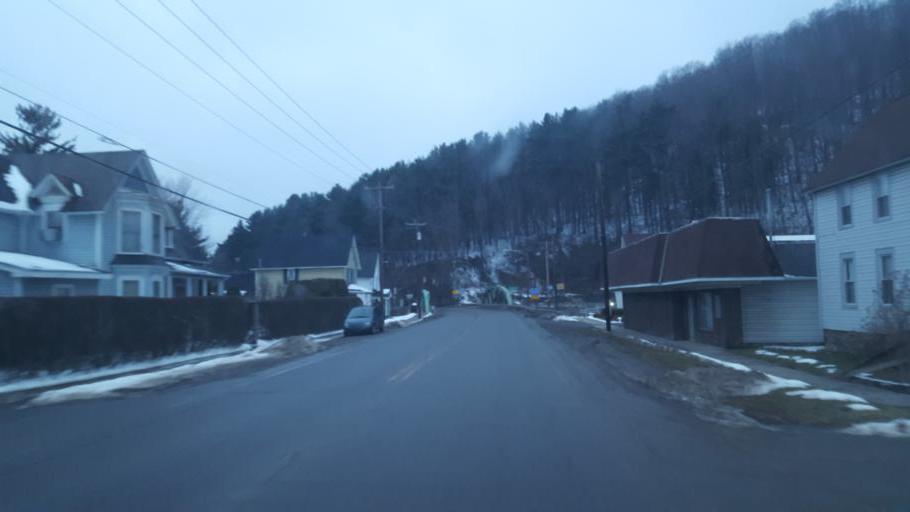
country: US
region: Pennsylvania
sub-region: Potter County
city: Coudersport
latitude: 41.7698
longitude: -78.0237
